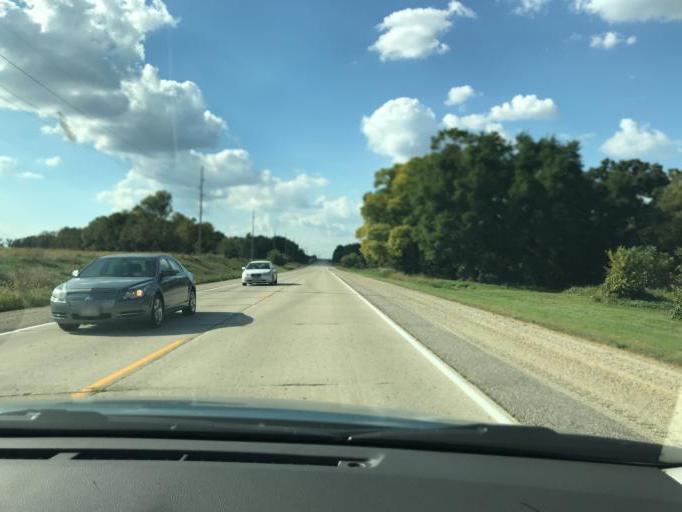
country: US
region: Wisconsin
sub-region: Rock County
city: Orfordville
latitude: 42.5489
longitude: -89.2726
